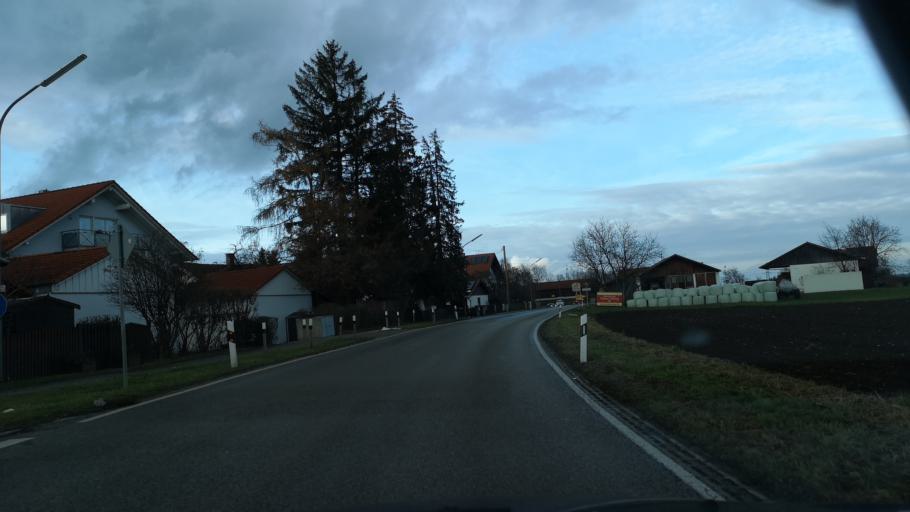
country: DE
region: Bavaria
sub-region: Upper Bavaria
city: Pliening
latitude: 48.1941
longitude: 11.8042
